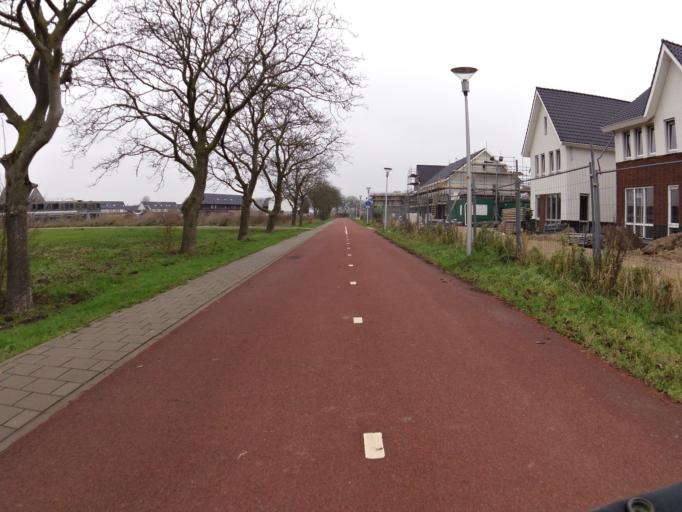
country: NL
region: Gelderland
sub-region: Gemeente Nijmegen
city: Nijmegen
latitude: 51.8715
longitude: 5.8646
